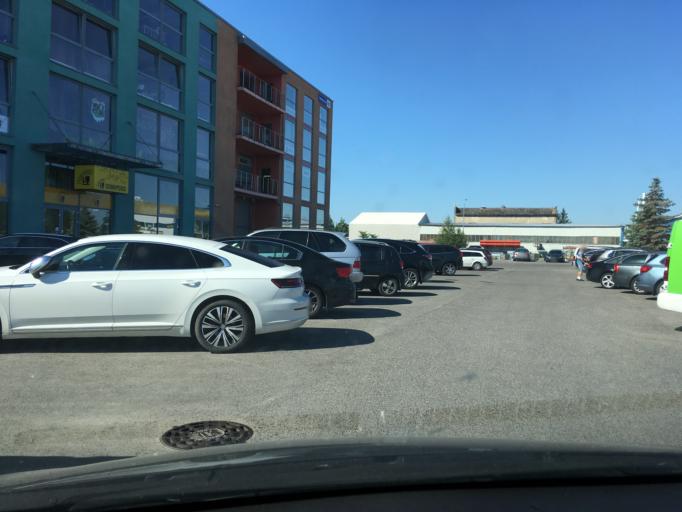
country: EE
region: Harju
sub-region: Tallinna linn
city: Kose
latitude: 59.4321
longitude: 24.8585
